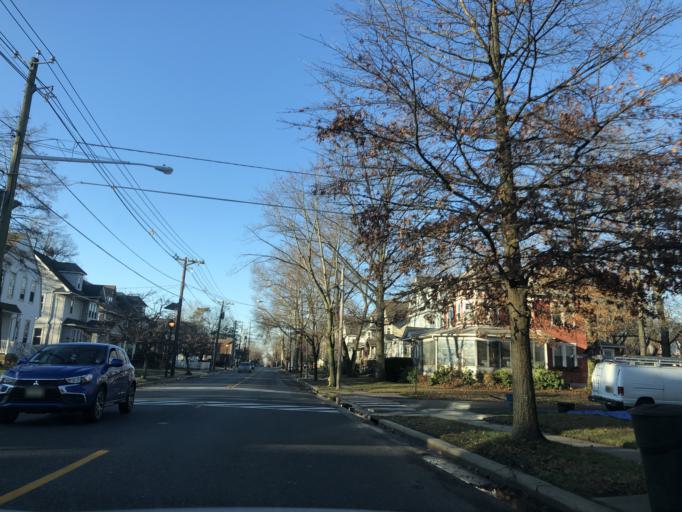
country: US
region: New Jersey
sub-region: Camden County
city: Oaklyn
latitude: 39.9095
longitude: -75.0889
